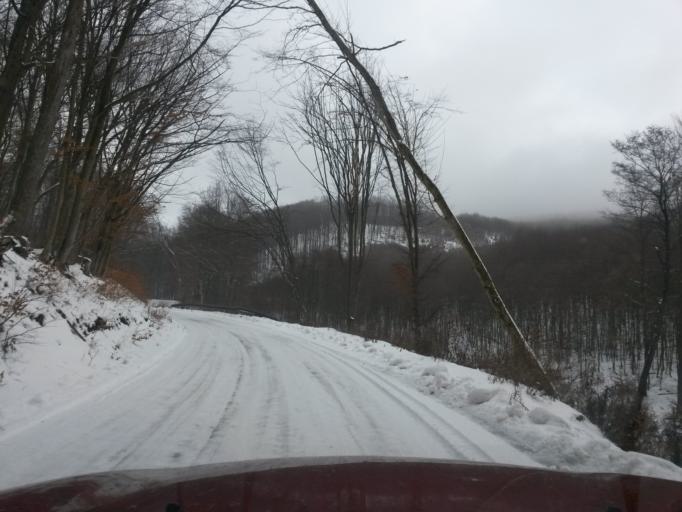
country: SK
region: Kosicky
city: Secovce
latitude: 48.8059
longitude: 21.5127
